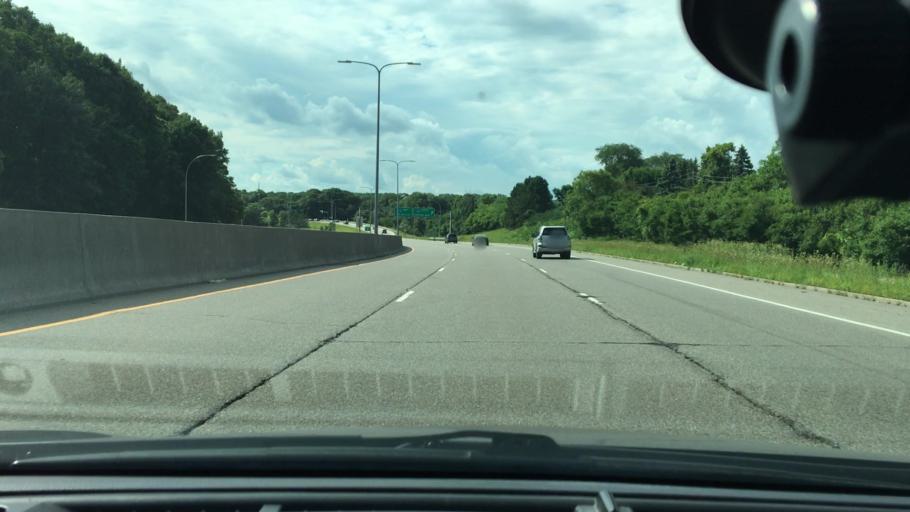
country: US
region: Minnesota
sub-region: Hennepin County
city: Wayzata
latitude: 44.9738
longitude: -93.4963
